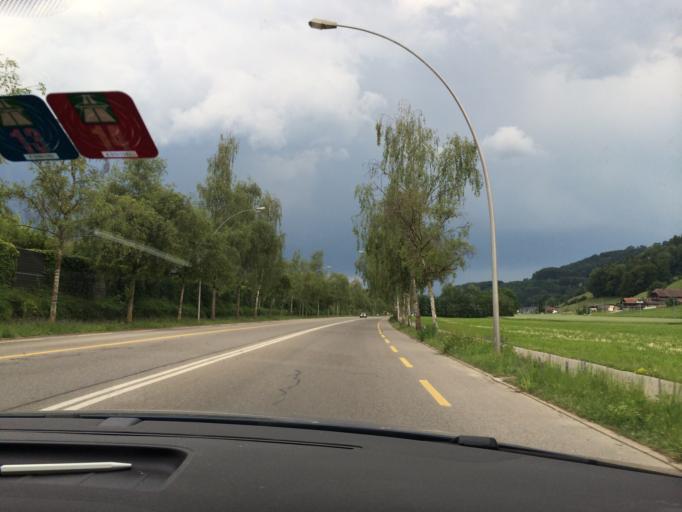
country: CH
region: Bern
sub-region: Bern-Mittelland District
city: Kehrsatz
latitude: 46.9219
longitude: 7.4620
